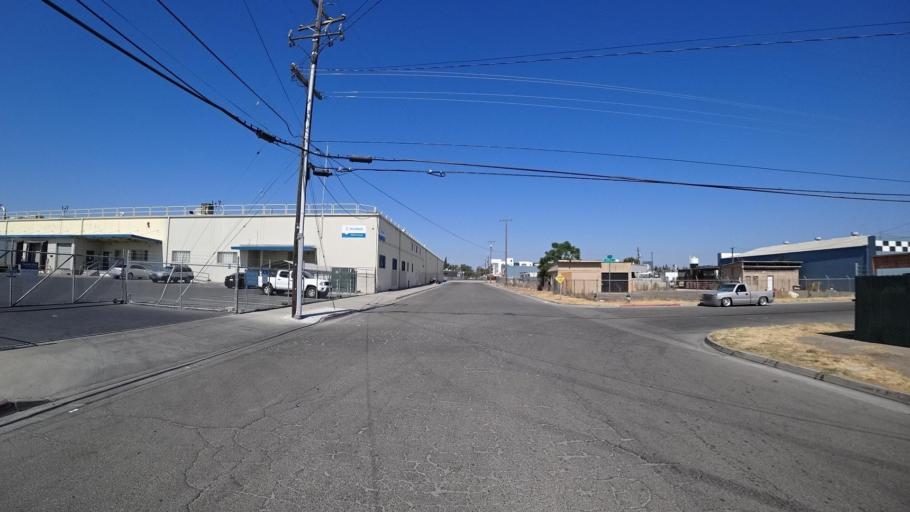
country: US
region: California
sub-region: Fresno County
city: Fresno
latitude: 36.7631
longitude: -119.7881
